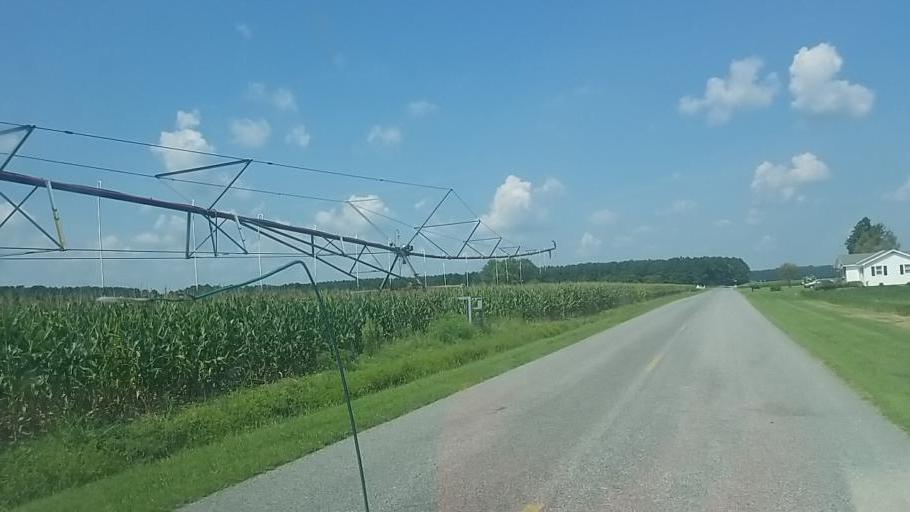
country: US
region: Maryland
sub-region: Worcester County
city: Berlin
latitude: 38.2962
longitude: -75.2622
